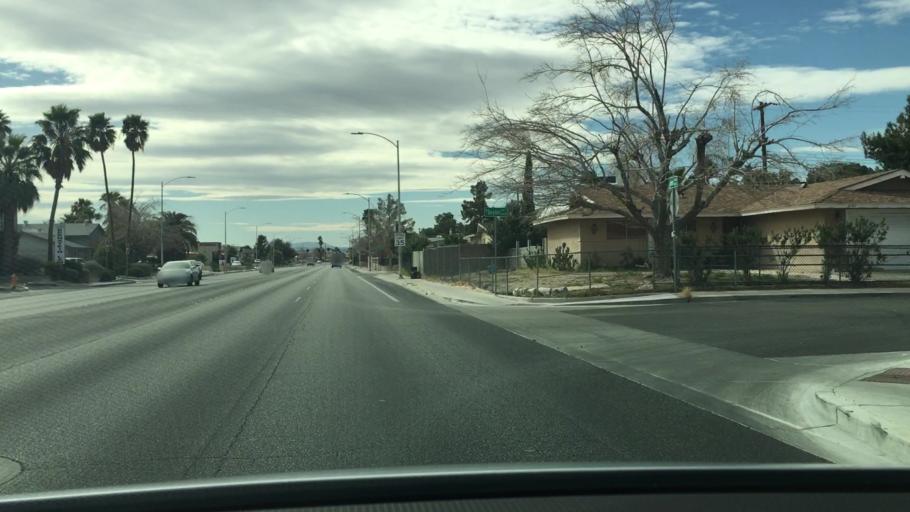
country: US
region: Nevada
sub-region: Clark County
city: Spring Valley
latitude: 36.1698
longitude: -115.2240
